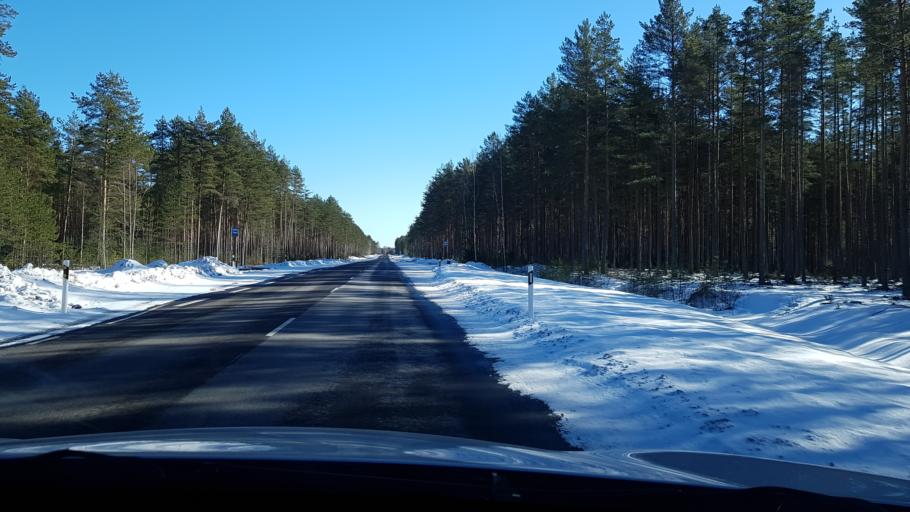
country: RU
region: Pskov
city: Pechory
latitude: 57.9666
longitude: 27.5987
